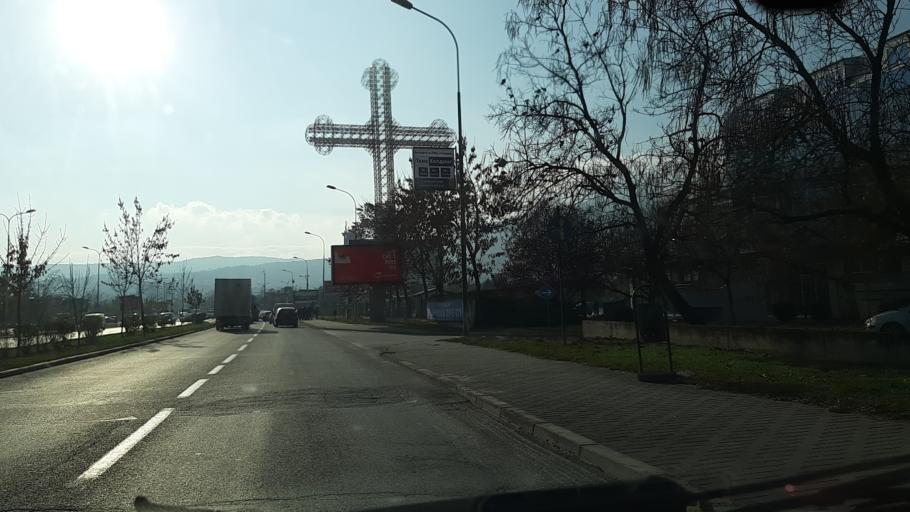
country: MK
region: Kisela Voda
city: Usje
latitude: 41.9786
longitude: 21.4662
